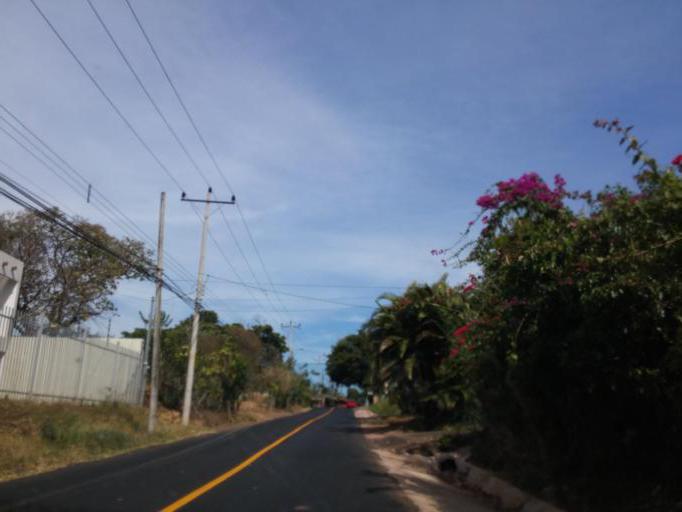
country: CR
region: Alajuela
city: Alajuela
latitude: 10.0283
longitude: -84.2241
